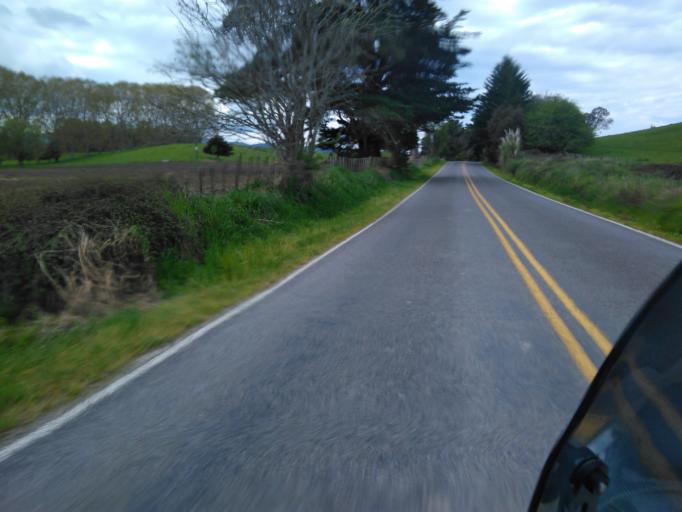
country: NZ
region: Hawke's Bay
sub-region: Wairoa District
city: Wairoa
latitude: -38.8961
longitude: 177.4586
